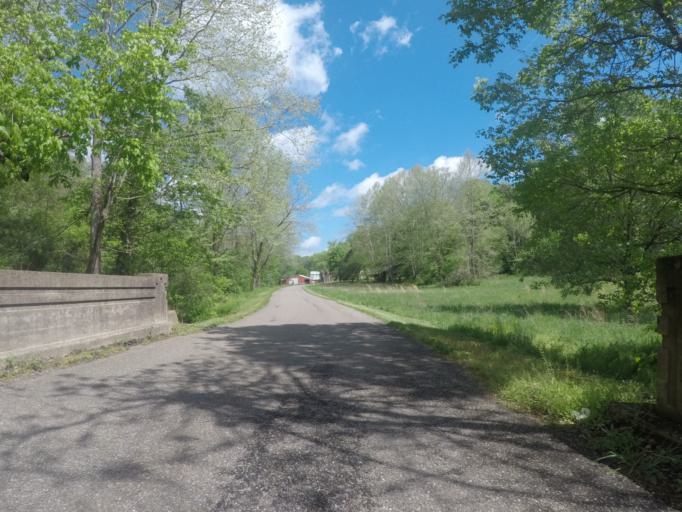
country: US
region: West Virginia
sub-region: Cabell County
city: Huntington
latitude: 38.5236
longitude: -82.4405
